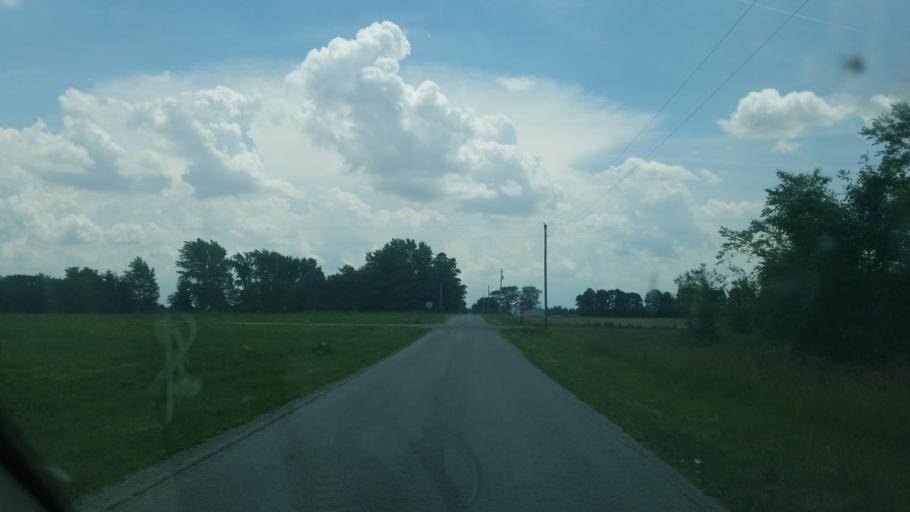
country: US
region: Ohio
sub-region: Hardin County
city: Forest
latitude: 40.7903
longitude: -83.6050
